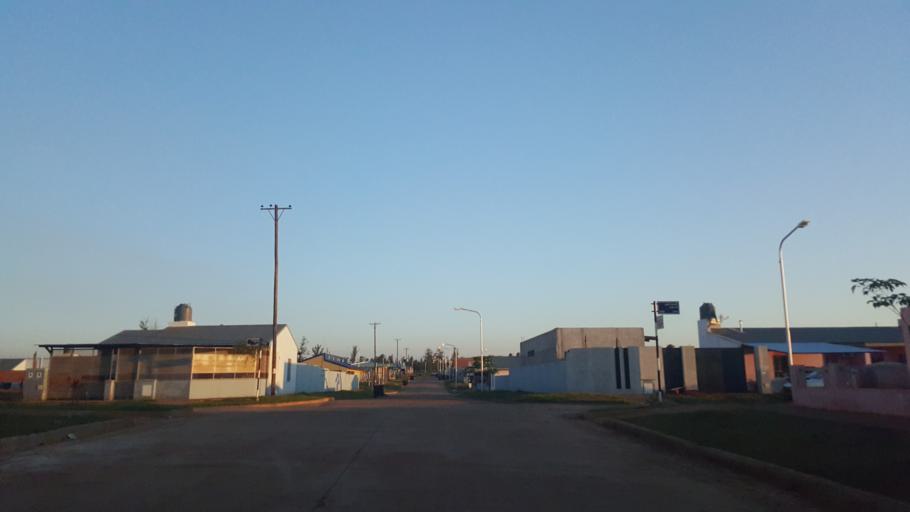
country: AR
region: Misiones
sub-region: Departamento de Capital
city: Posadas
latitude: -27.4110
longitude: -55.9861
